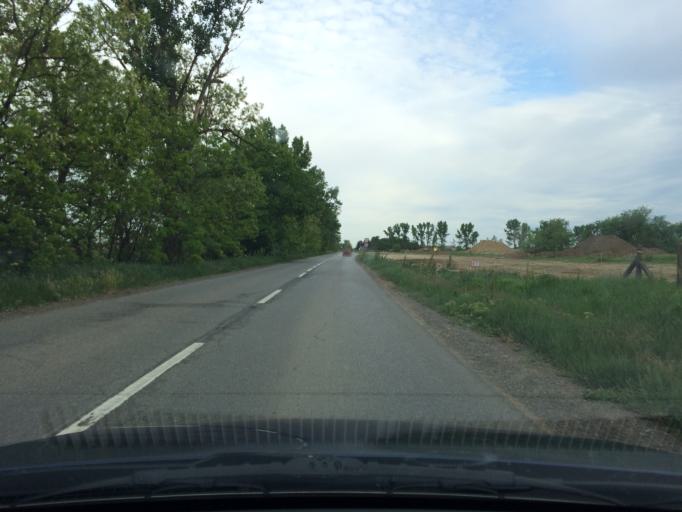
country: HU
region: Szabolcs-Szatmar-Bereg
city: Tiszavasvari
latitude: 47.9356
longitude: 21.3830
